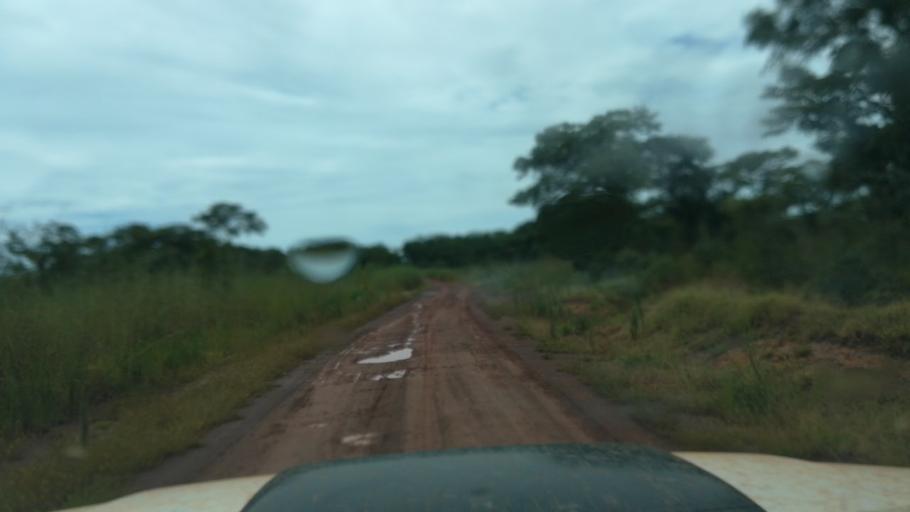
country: ZM
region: Luapula
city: Mwense
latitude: -10.0223
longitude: 28.1201
